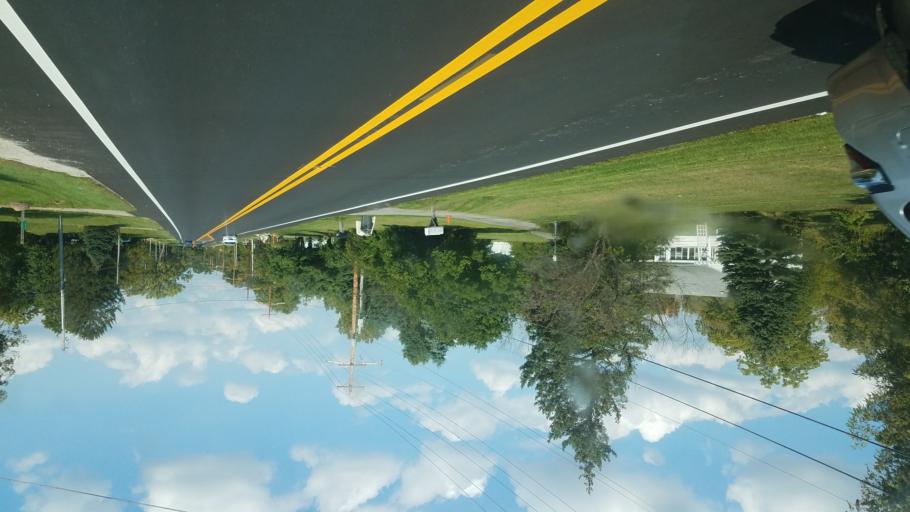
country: US
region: Ohio
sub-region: Franklin County
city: Grove City
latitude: 39.9144
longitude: -83.1056
